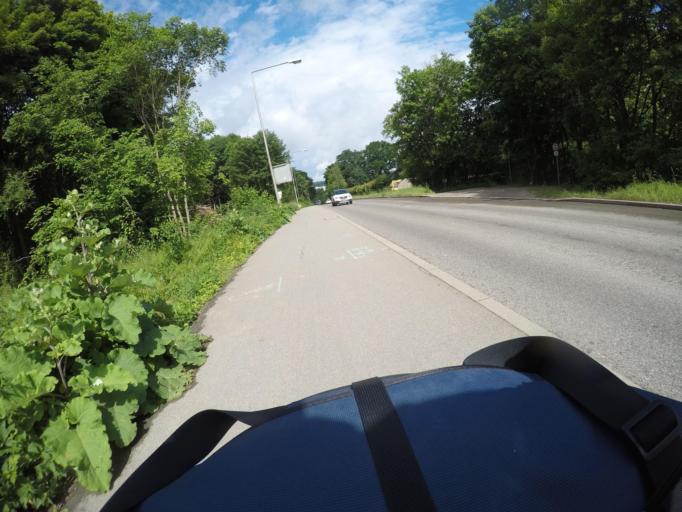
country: DE
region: Baden-Wuerttemberg
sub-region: Regierungsbezirk Stuttgart
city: Gerlingen
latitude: 48.7401
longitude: 9.0902
